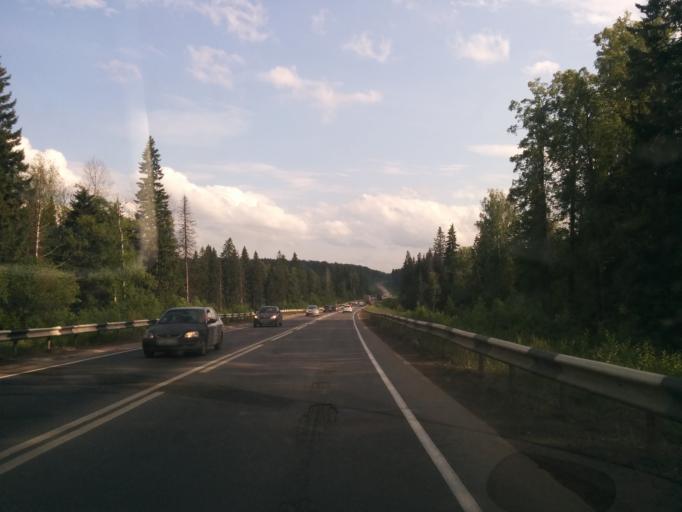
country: RU
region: Perm
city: Novyye Lyady
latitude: 58.0937
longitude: 56.4267
